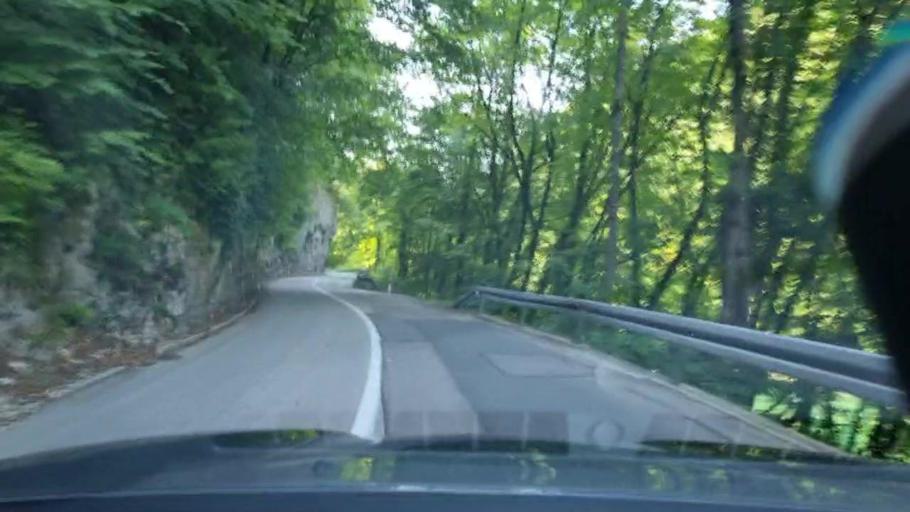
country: BA
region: Federation of Bosnia and Herzegovina
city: Stijena
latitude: 44.8894
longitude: 16.0537
